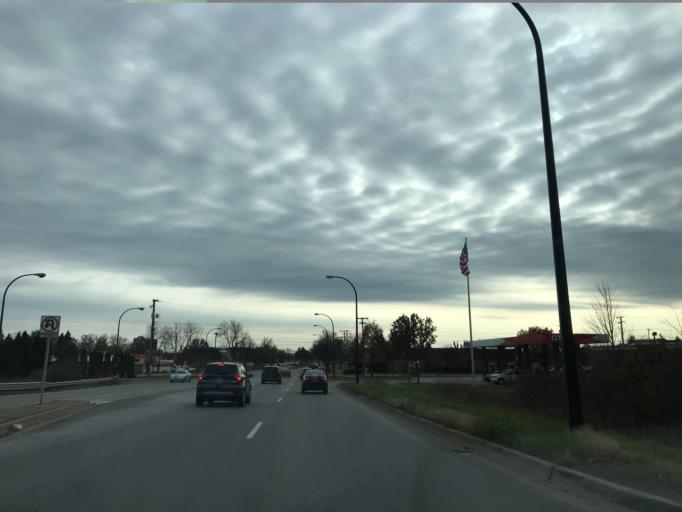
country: US
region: Michigan
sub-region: Washtenaw County
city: Ann Arbor
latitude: 42.2356
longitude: -83.7392
